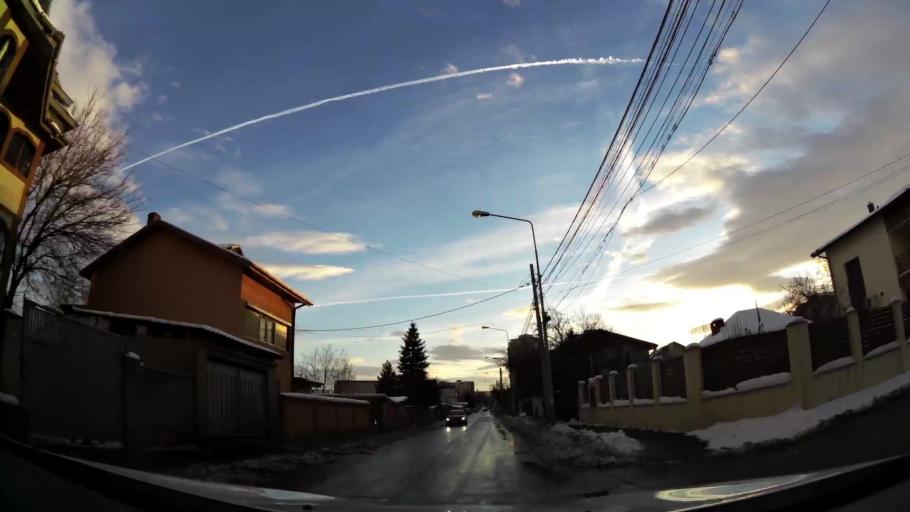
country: RO
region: Ilfov
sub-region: Comuna Popesti-Leordeni
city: Popesti-Leordeni
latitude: 44.3745
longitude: 26.1443
